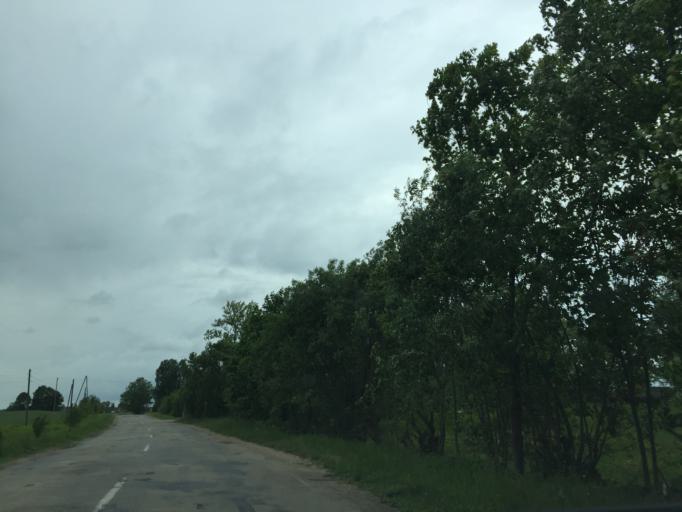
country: LV
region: Varkava
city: Vecvarkava
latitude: 56.0985
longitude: 26.5356
